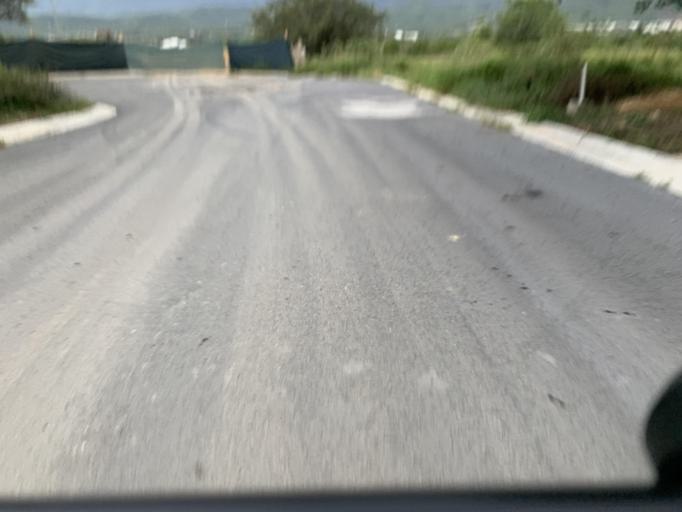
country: MX
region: Nuevo Leon
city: Santiago
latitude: 25.5058
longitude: -100.1789
